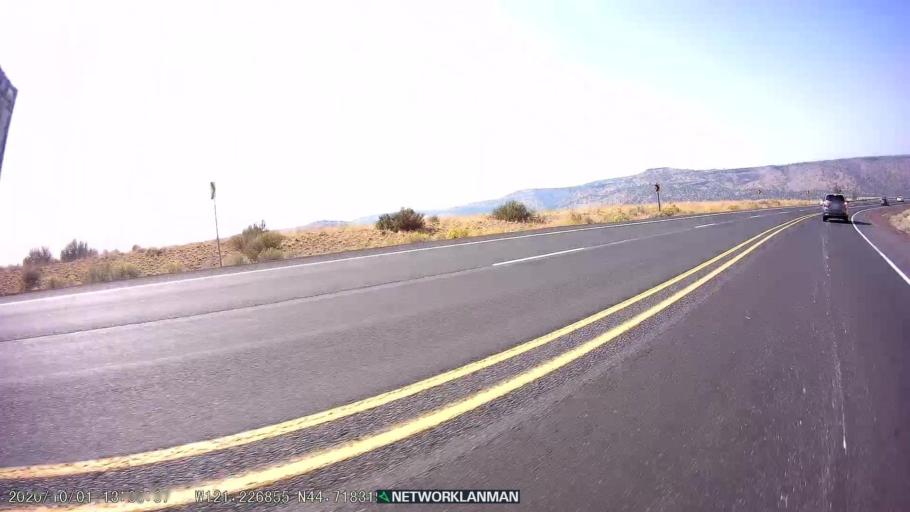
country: US
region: Oregon
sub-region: Jefferson County
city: Warm Springs
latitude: 44.7183
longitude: -121.2275
